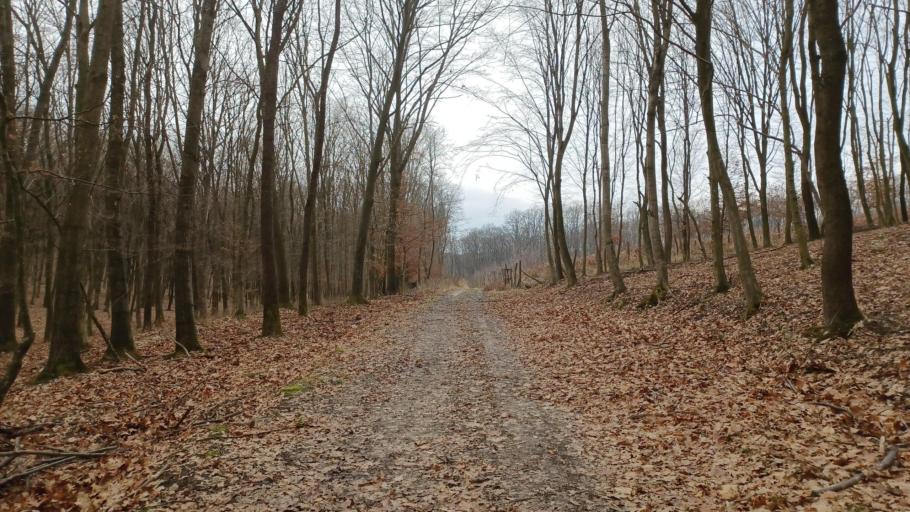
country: HU
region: Tolna
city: Szentgalpuszta
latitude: 46.3066
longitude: 18.6405
